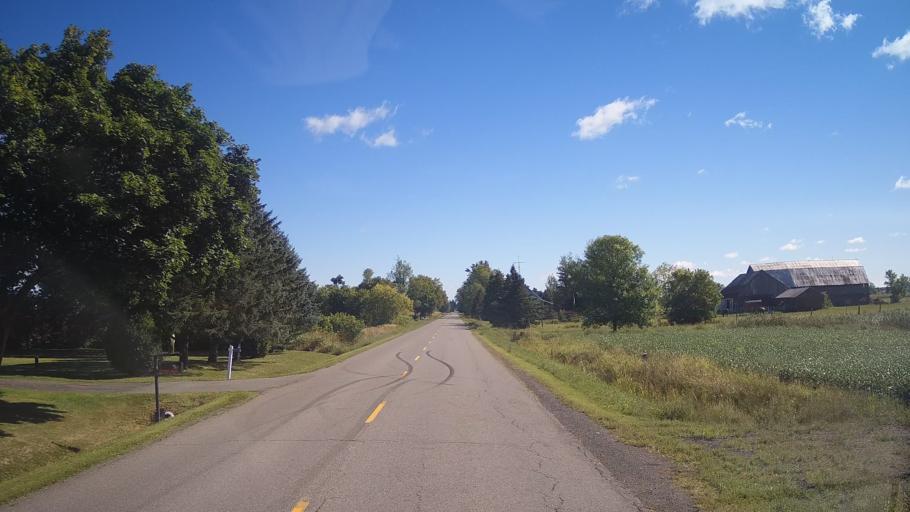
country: CA
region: Ontario
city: Prescott
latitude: 44.9067
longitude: -75.3872
